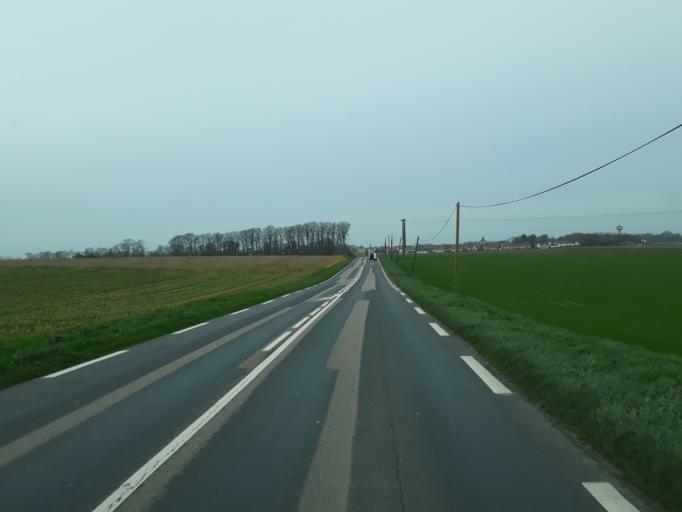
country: FR
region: Haute-Normandie
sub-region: Departement de la Seine-Maritime
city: Breaute
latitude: 49.6167
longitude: 0.4065
